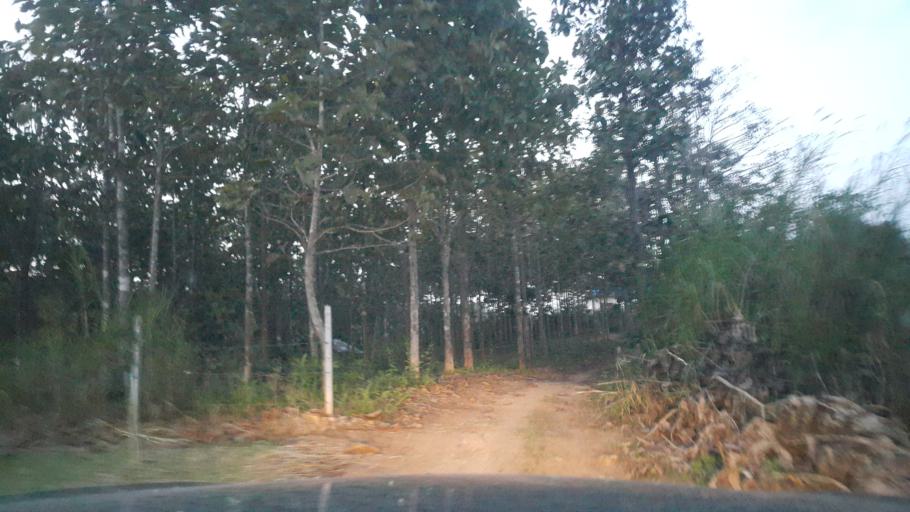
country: TH
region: Chiang Mai
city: Samoeng
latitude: 18.9520
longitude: 98.6721
